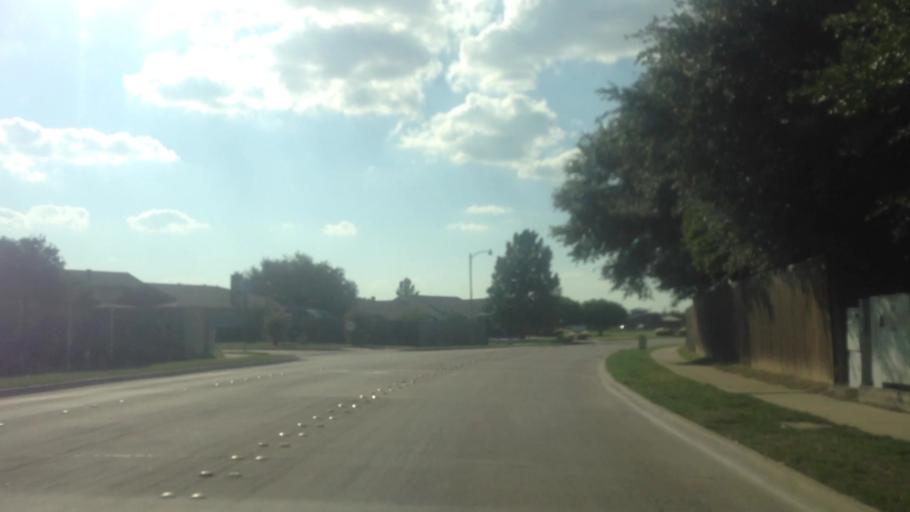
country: US
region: Texas
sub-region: Tarrant County
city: Watauga
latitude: 32.8851
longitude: -97.2555
